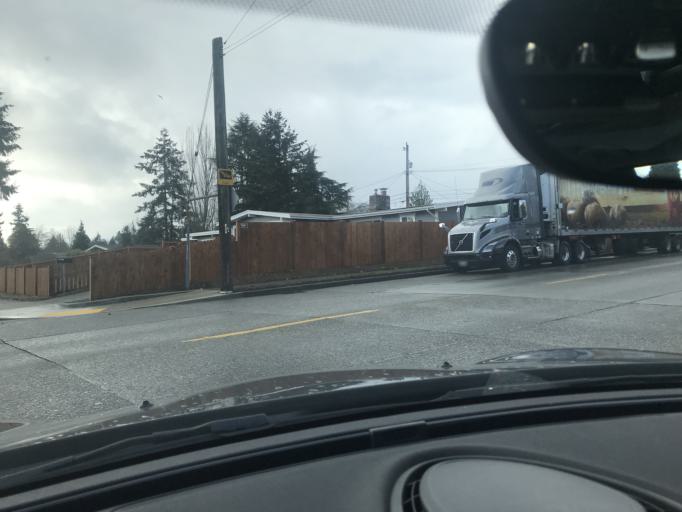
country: US
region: Washington
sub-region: King County
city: White Center
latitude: 47.5211
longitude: -122.3700
